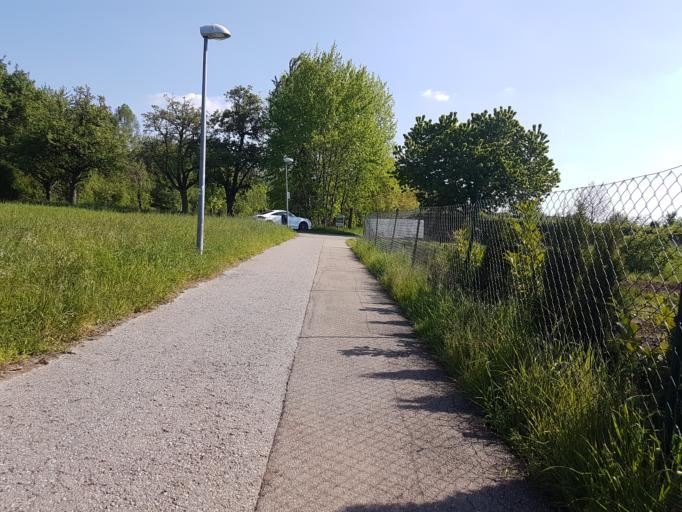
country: DE
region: Baden-Wuerttemberg
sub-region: Regierungsbezirk Stuttgart
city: Ludwigsburg
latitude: 48.9022
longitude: 9.1719
